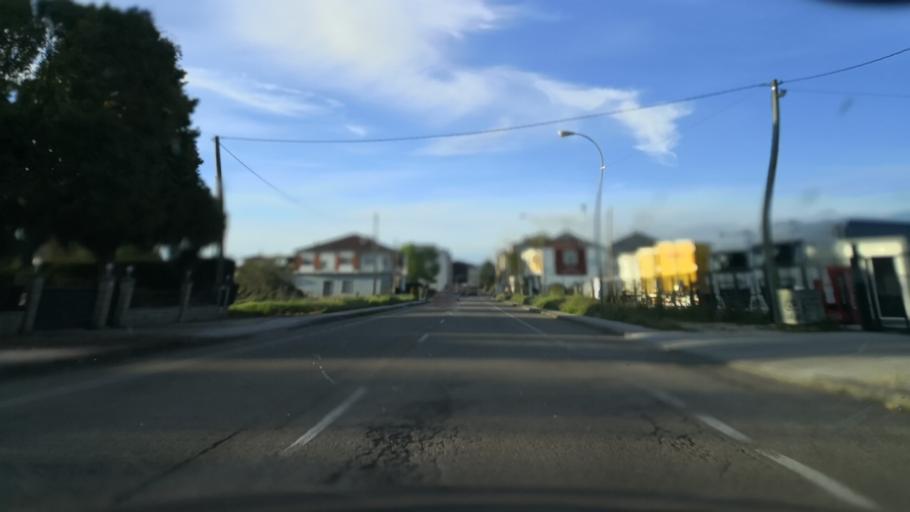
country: ES
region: Galicia
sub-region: Provincia de Ourense
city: Verin
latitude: 41.9288
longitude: -7.4412
